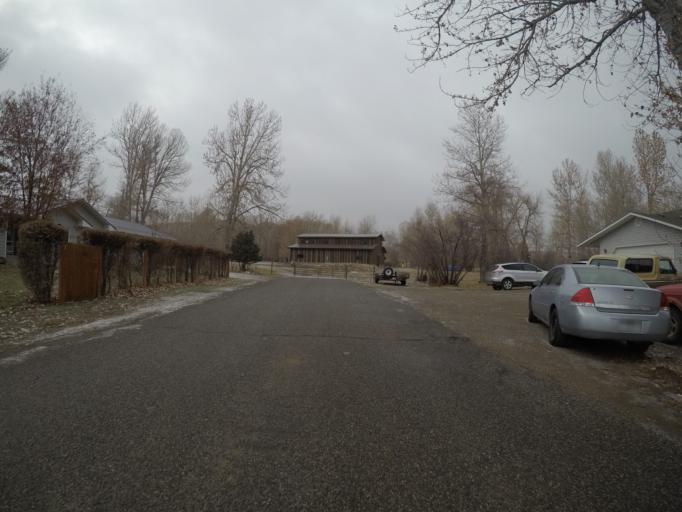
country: US
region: Montana
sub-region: Stillwater County
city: Absarokee
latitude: 45.5235
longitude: -109.4416
